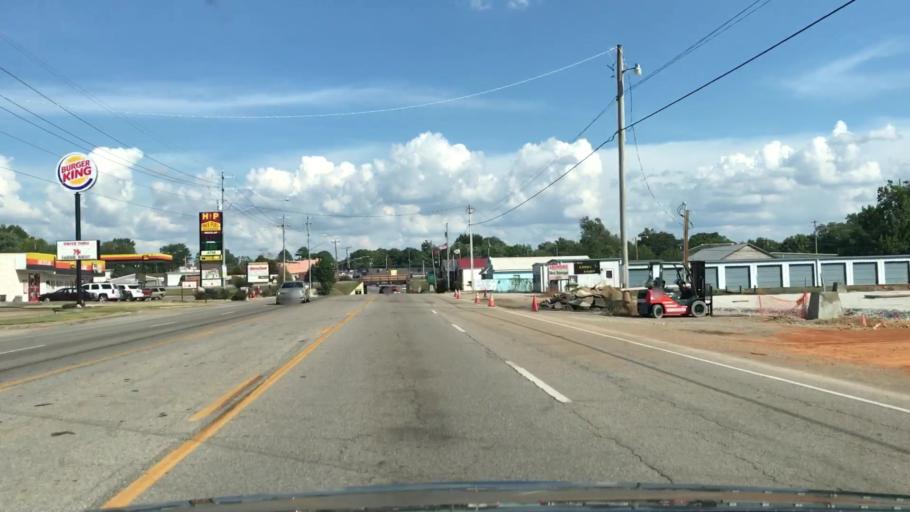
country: US
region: Alabama
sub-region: Limestone County
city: Ardmore
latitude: 34.9929
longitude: -86.8493
